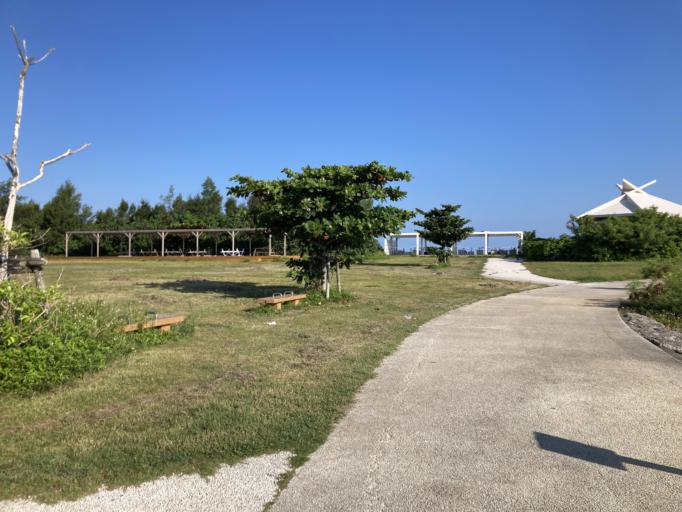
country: JP
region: Okinawa
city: Naha-shi
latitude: 26.2207
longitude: 127.6648
